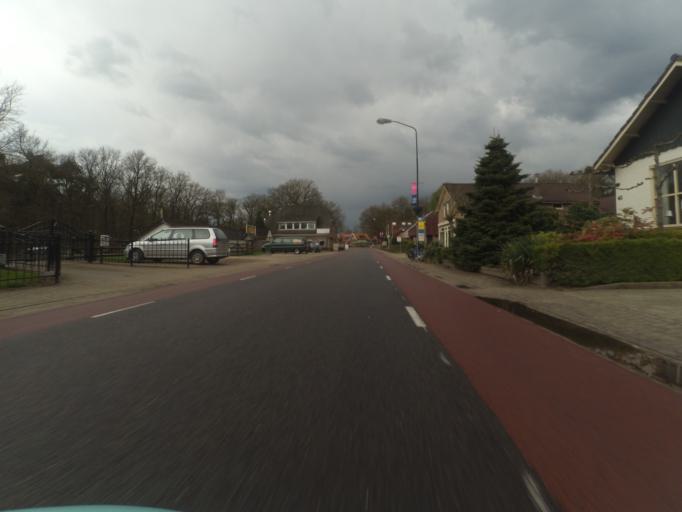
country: NL
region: Gelderland
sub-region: Gemeente Apeldoorn
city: Beekbergen
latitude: 52.1190
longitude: 5.8849
